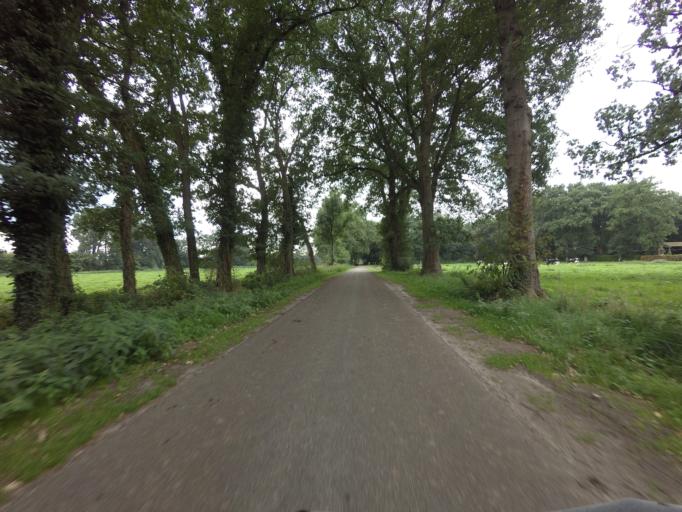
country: DE
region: Lower Saxony
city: Lage
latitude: 52.4681
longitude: 6.9305
